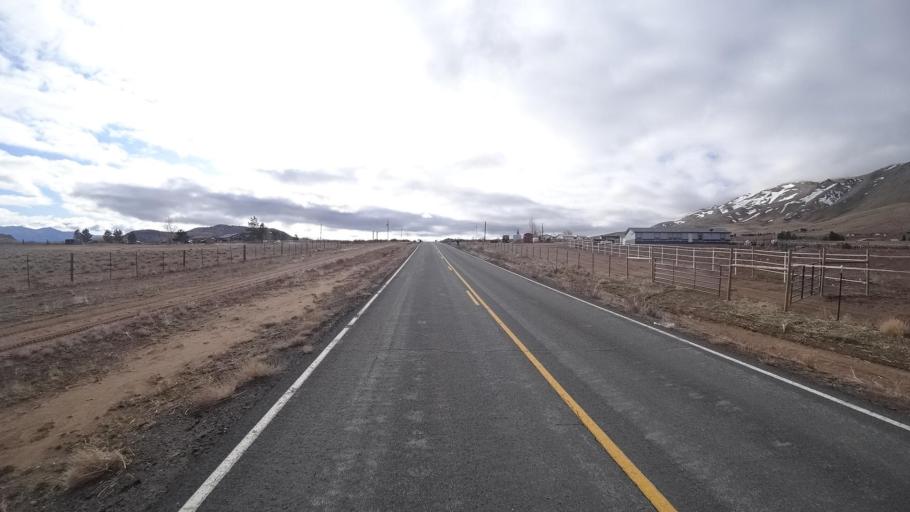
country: US
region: Nevada
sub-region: Washoe County
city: Cold Springs
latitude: 39.8924
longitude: -119.9779
